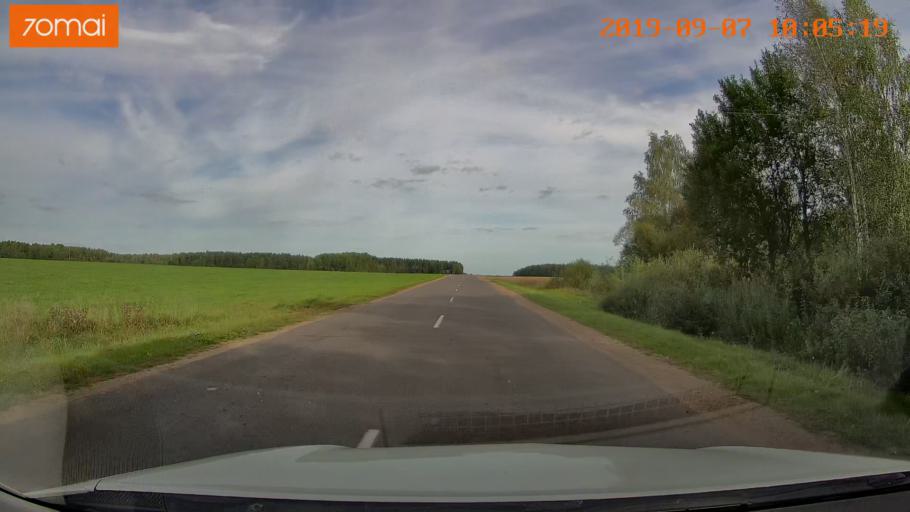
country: BY
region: Grodnenskaya
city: Voranava
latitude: 54.0457
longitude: 25.4081
